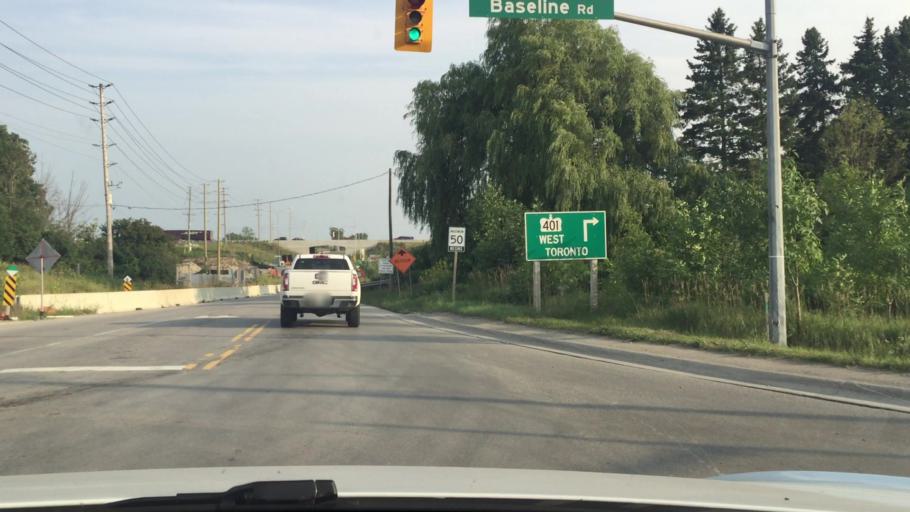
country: CA
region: Ontario
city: Oshawa
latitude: 43.8813
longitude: -78.7647
